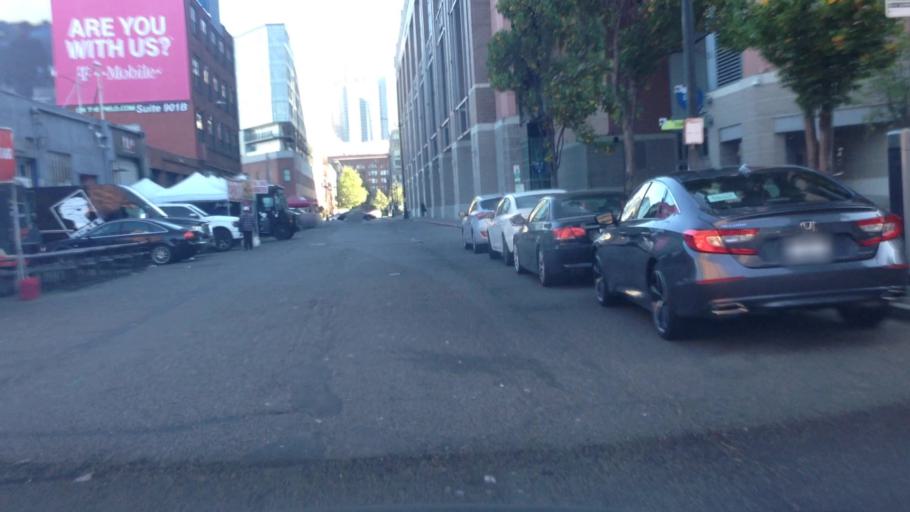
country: US
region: Washington
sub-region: King County
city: Seattle
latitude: 47.5941
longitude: -122.3332
